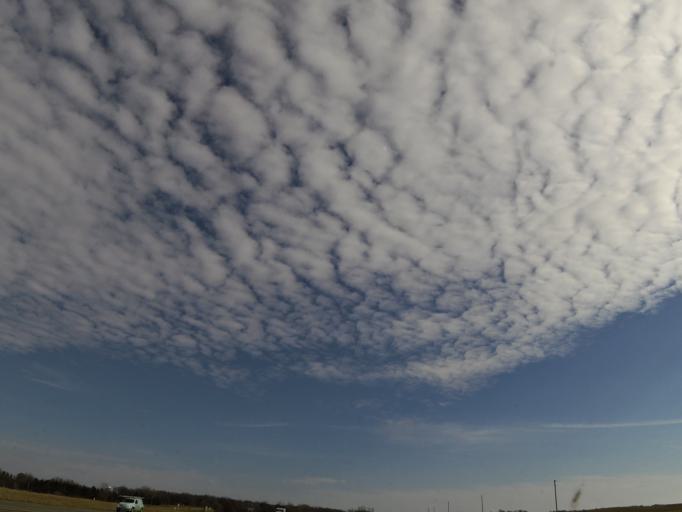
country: US
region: Minnesota
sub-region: Steele County
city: Medford
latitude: 44.2052
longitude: -93.2605
